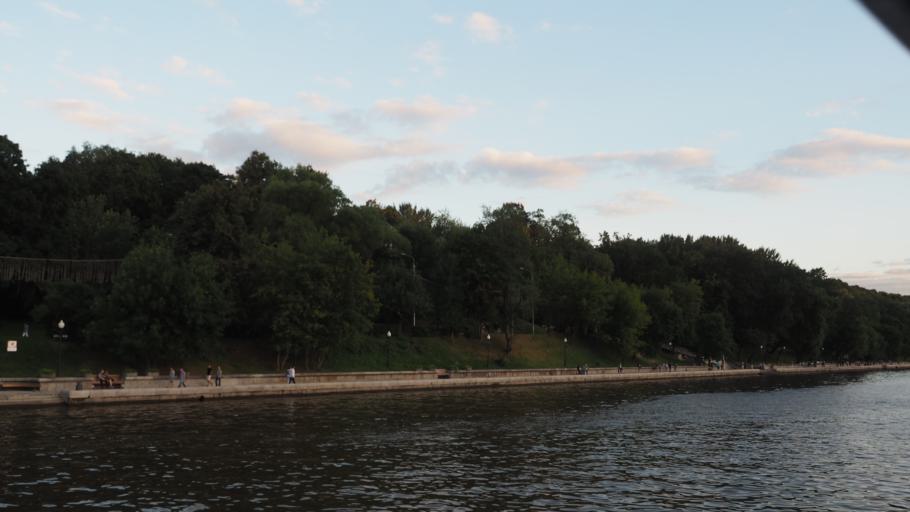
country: RU
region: Moscow
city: Novyye Cheremushki
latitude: 55.7207
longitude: 37.5875
